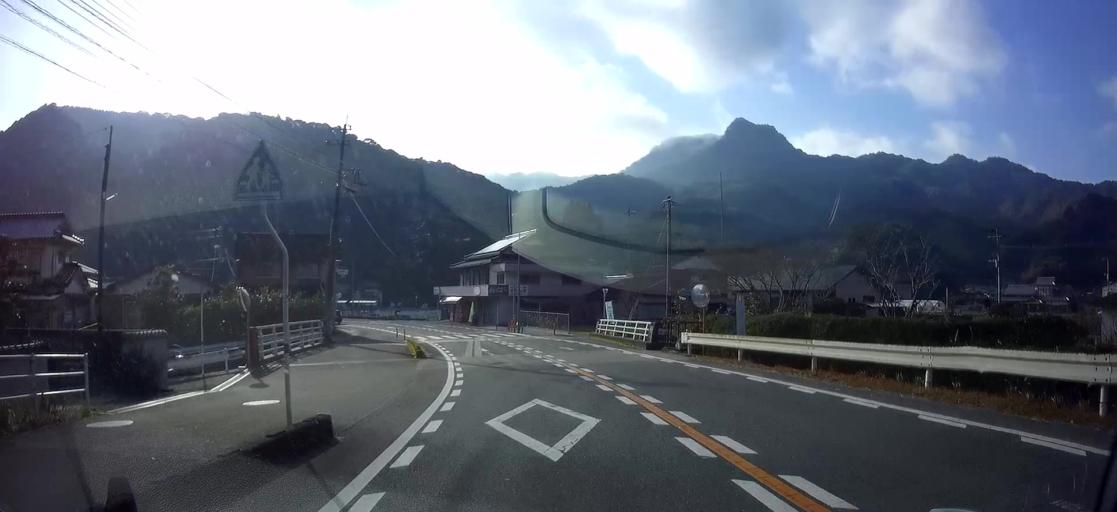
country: JP
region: Kumamoto
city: Hondo
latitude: 32.4317
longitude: 130.4001
